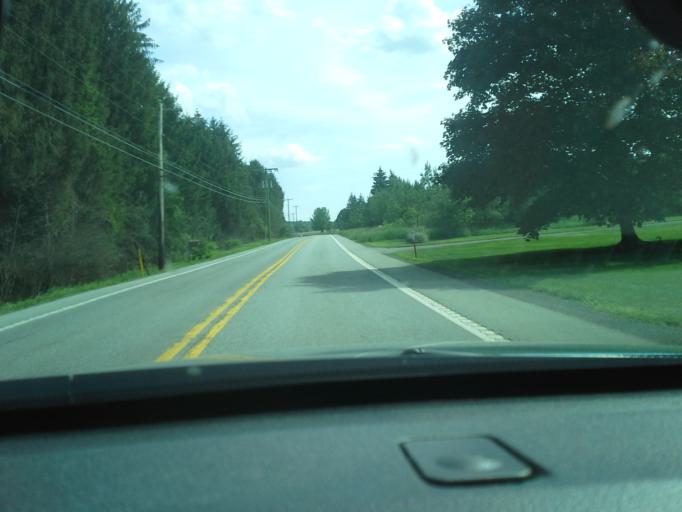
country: US
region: Pennsylvania
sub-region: Fulton County
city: McConnellsburg
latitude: 39.9926
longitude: -77.9661
